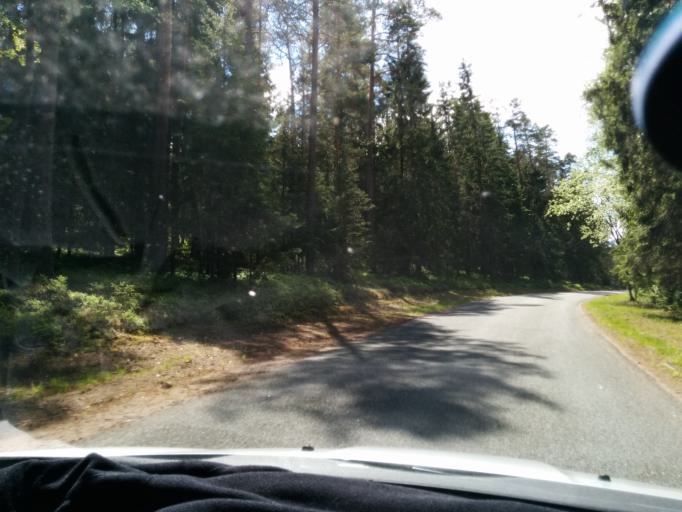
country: EE
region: Laeaene-Virumaa
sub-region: Kadrina vald
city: Kadrina
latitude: 59.5565
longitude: 25.9936
